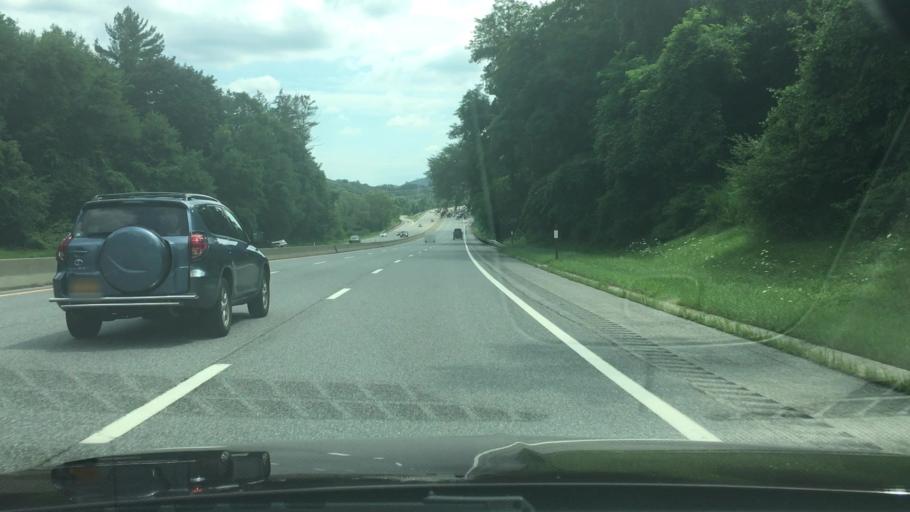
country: US
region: New York
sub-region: Westchester County
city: Briarcliff Manor
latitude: 41.1527
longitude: -73.8164
